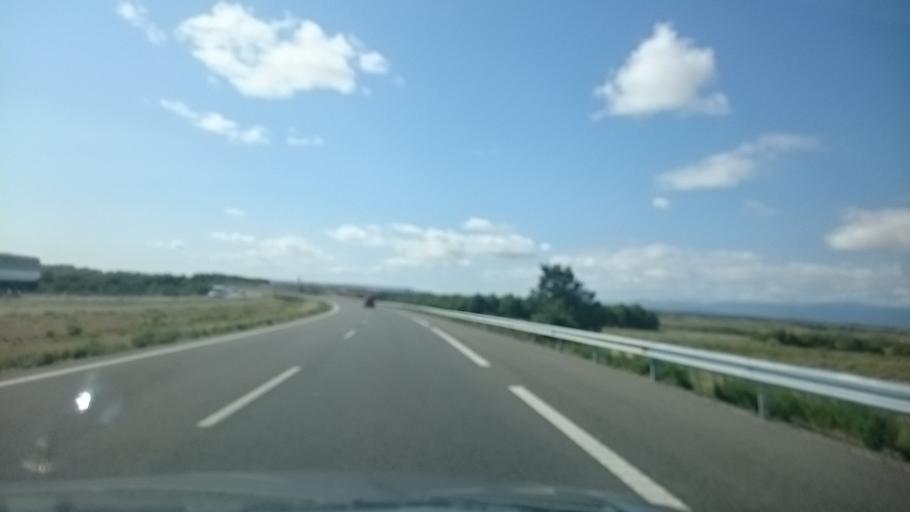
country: ES
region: Navarre
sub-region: Provincia de Navarra
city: Murchante
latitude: 42.0588
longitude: -1.6894
